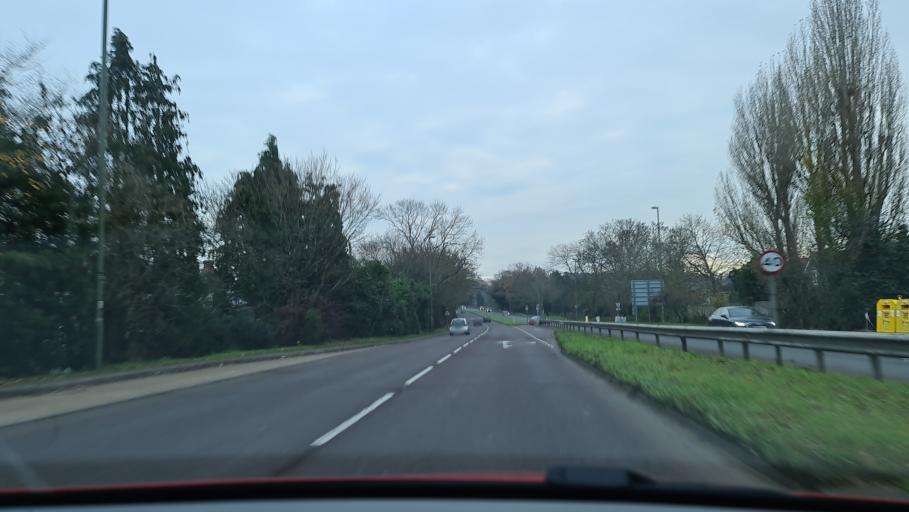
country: GB
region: England
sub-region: Surrey
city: Hinchley Wood
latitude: 51.3773
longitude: -0.3459
